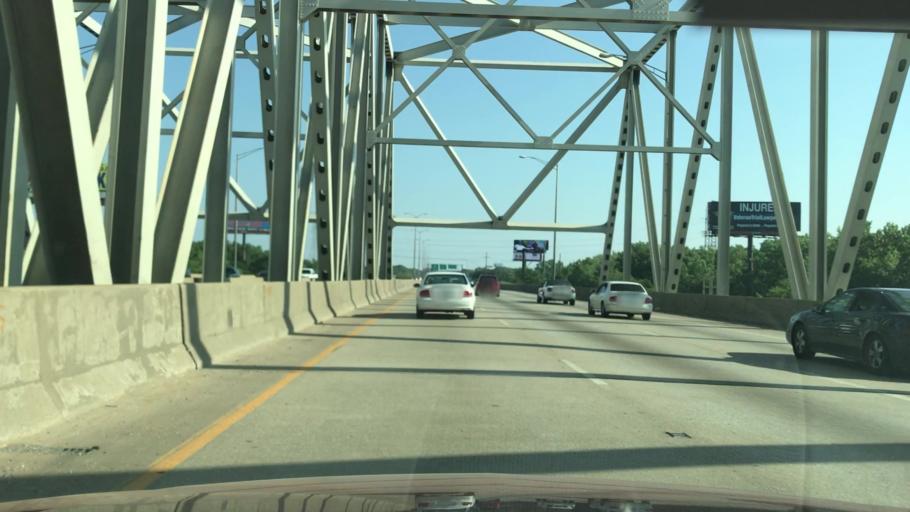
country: US
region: Illinois
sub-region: Cook County
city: Burnham
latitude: 41.6411
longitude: -87.5786
